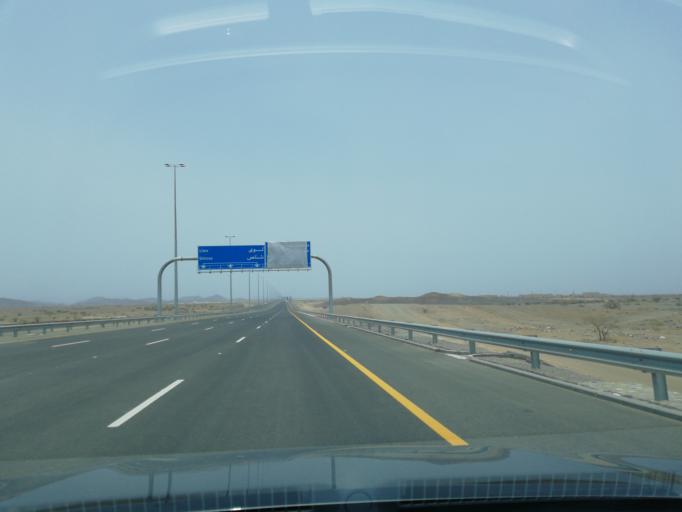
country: OM
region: Al Batinah
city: Al Liwa'
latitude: 24.4337
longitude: 56.5254
